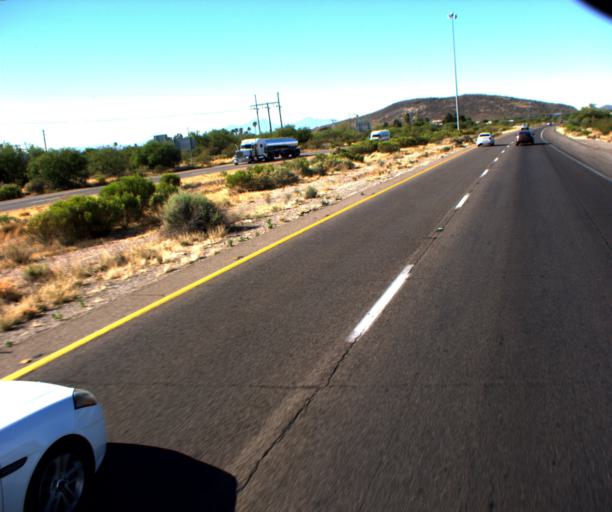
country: US
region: Arizona
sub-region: Pima County
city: Drexel Heights
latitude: 32.1273
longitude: -110.9870
